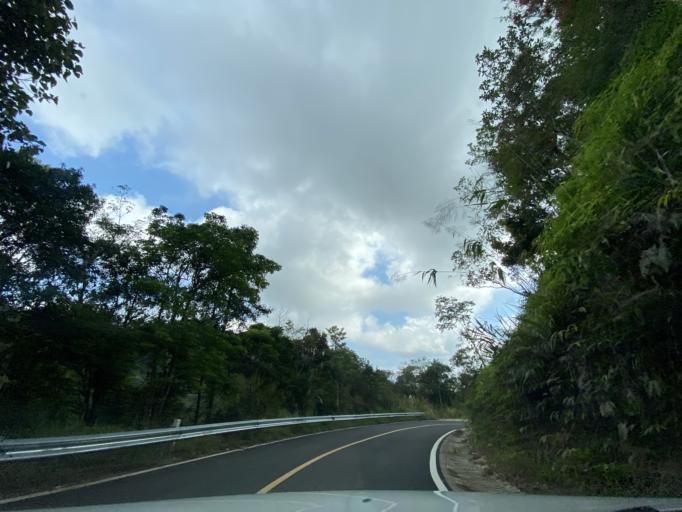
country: CN
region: Hainan
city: Diaoluoshan
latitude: 18.7055
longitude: 109.8825
